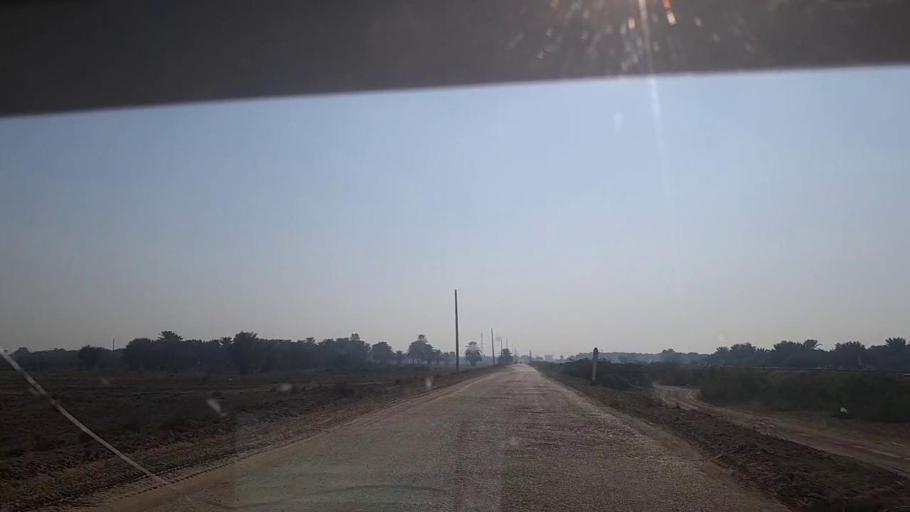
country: PK
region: Sindh
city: Gambat
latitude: 27.3527
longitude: 68.5513
